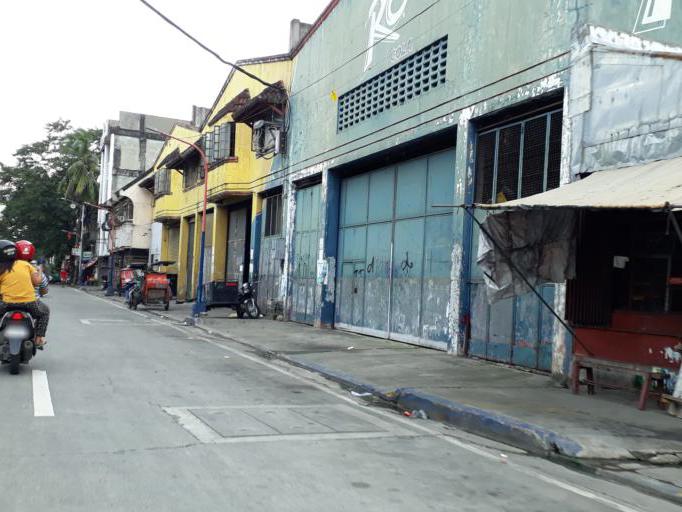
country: PH
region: Metro Manila
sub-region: City of Manila
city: Manila
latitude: 14.6072
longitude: 120.9994
